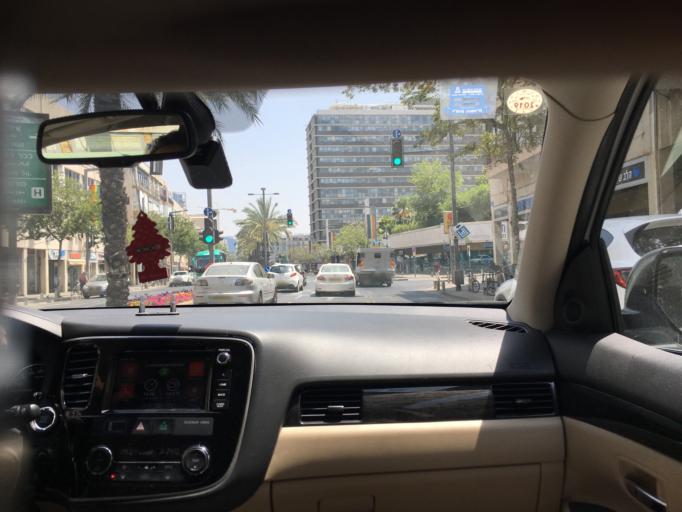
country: IL
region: Tel Aviv
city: Tel Aviv
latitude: 32.0835
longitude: 34.7813
